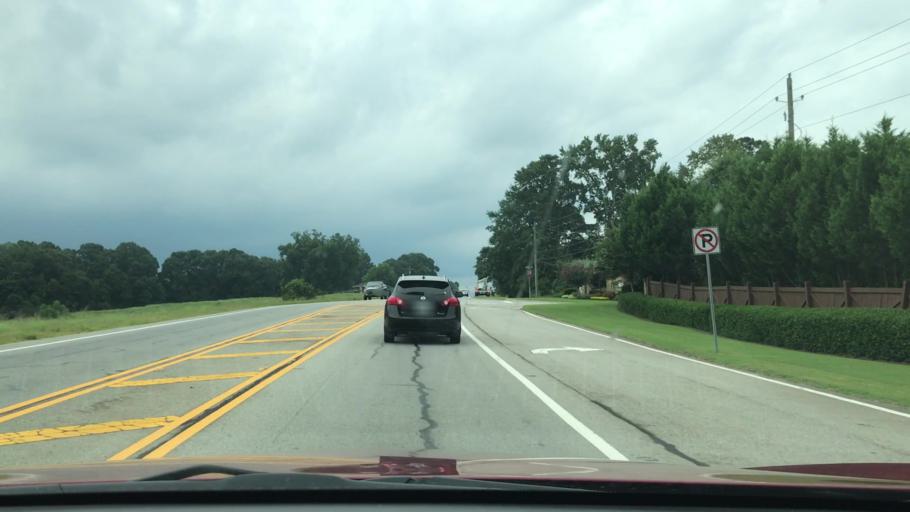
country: US
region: Georgia
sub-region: Jackson County
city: Hoschton
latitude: 34.0484
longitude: -83.7779
